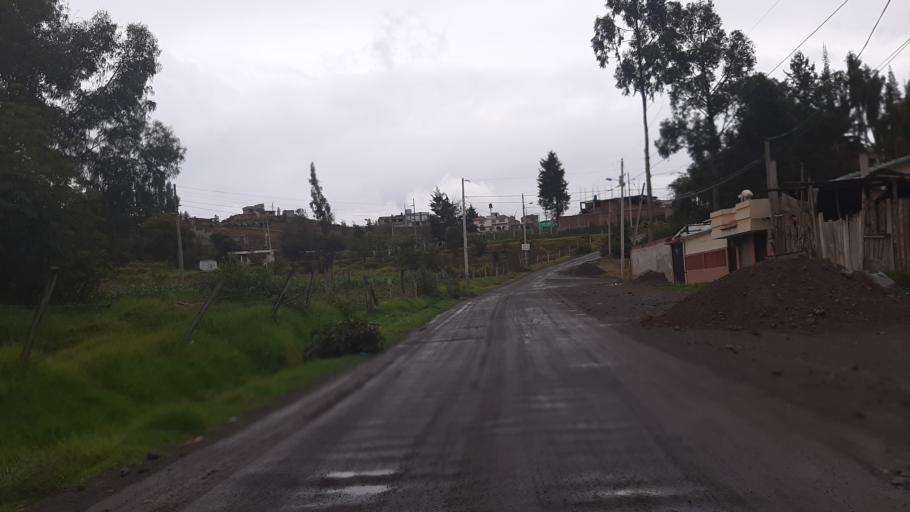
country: EC
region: Chimborazo
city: Riobamba
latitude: -1.6495
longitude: -78.6392
